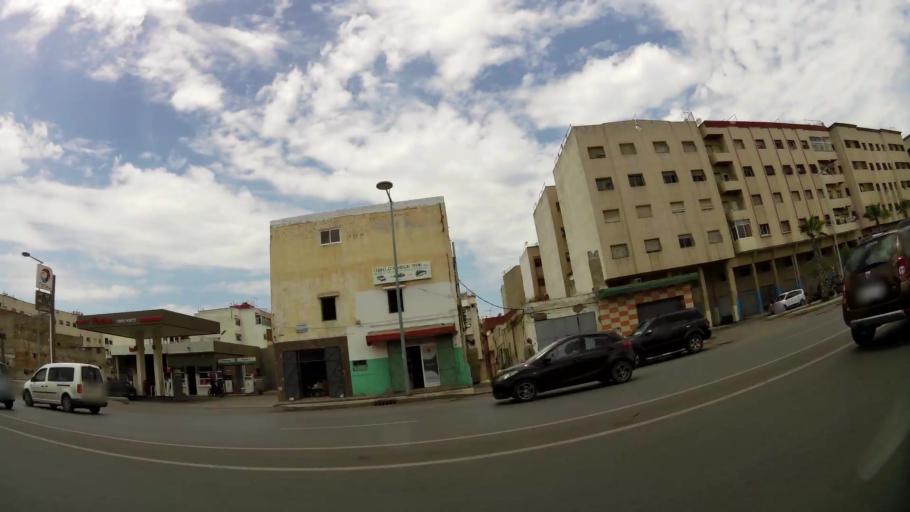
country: MA
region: Rabat-Sale-Zemmour-Zaer
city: Sale
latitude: 34.0497
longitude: -6.8142
